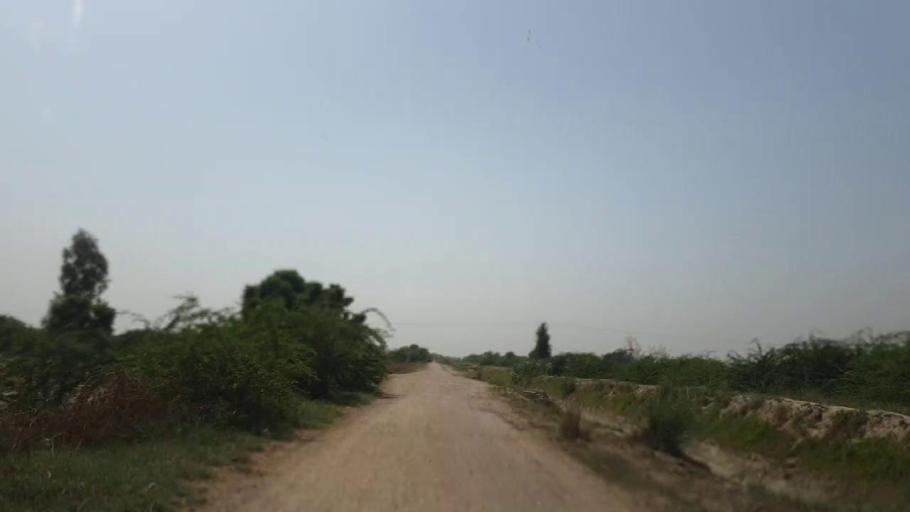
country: PK
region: Sindh
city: Jhol
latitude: 25.8635
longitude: 69.0335
